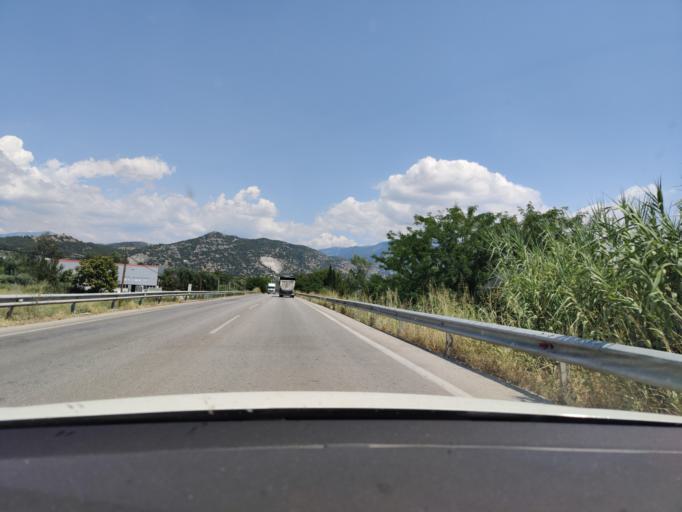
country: GR
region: Central Macedonia
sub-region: Nomos Serron
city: Serres
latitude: 41.0837
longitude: 23.5743
